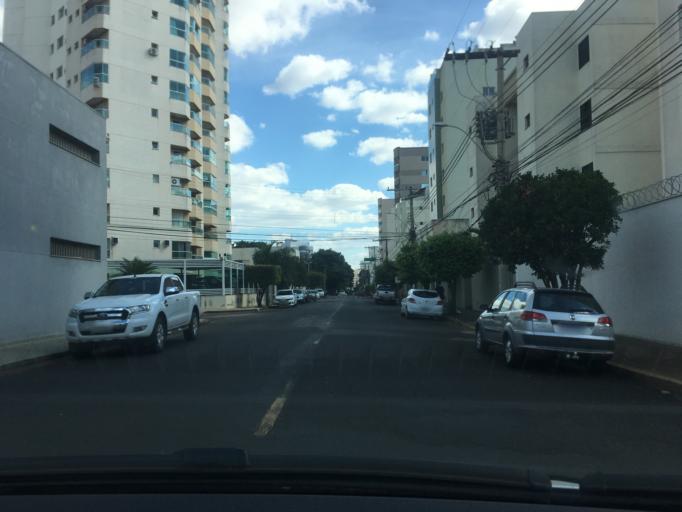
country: BR
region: Minas Gerais
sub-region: Uberlandia
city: Uberlandia
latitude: -18.9141
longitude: -48.2594
